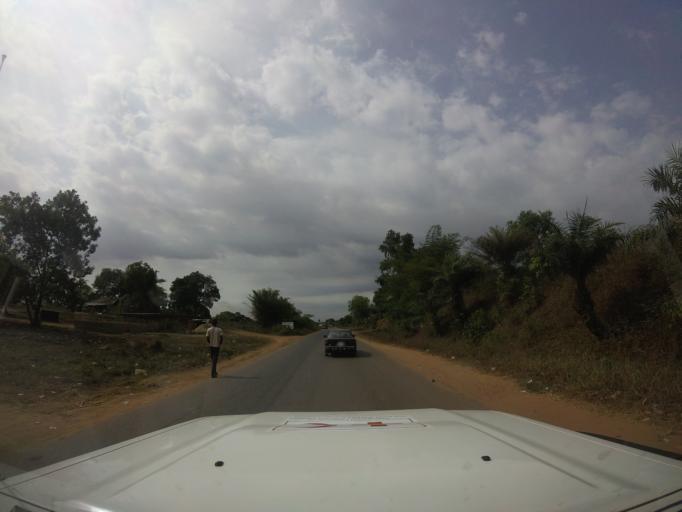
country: LR
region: Montserrado
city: Monrovia
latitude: 6.4783
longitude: -10.8118
